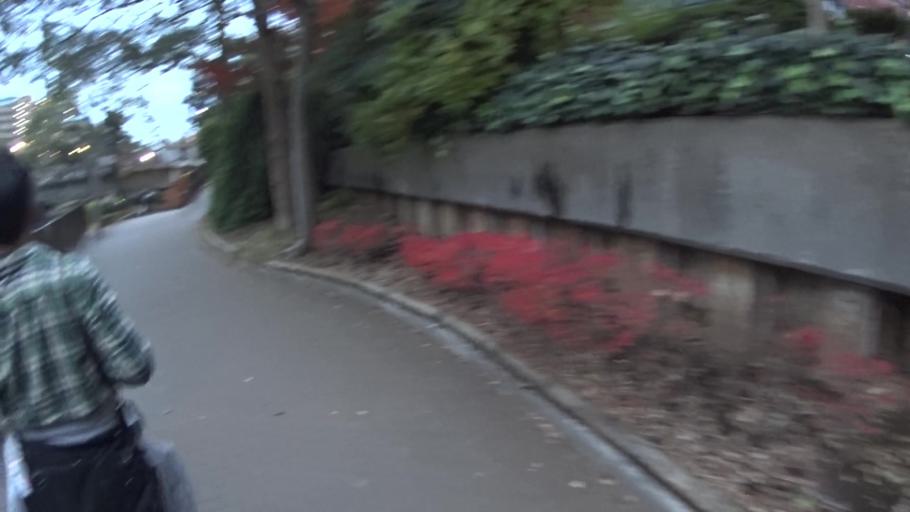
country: JP
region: Tokyo
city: Urayasu
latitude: 35.6790
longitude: 139.8203
